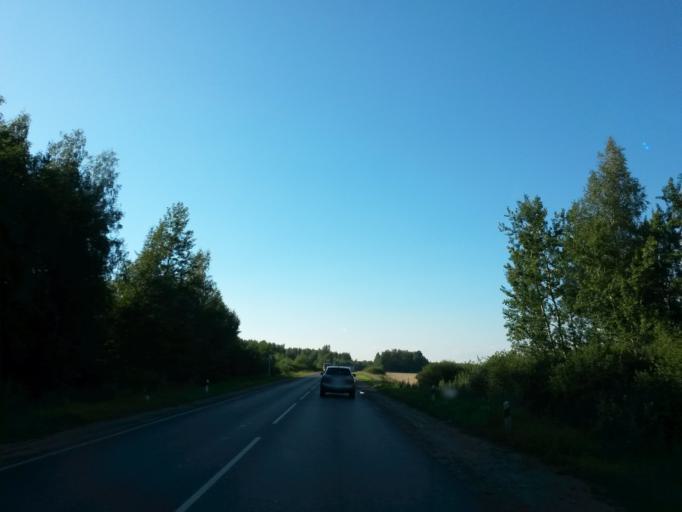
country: RU
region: Ivanovo
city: Novo-Talitsy
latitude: 57.0309
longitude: 40.7525
